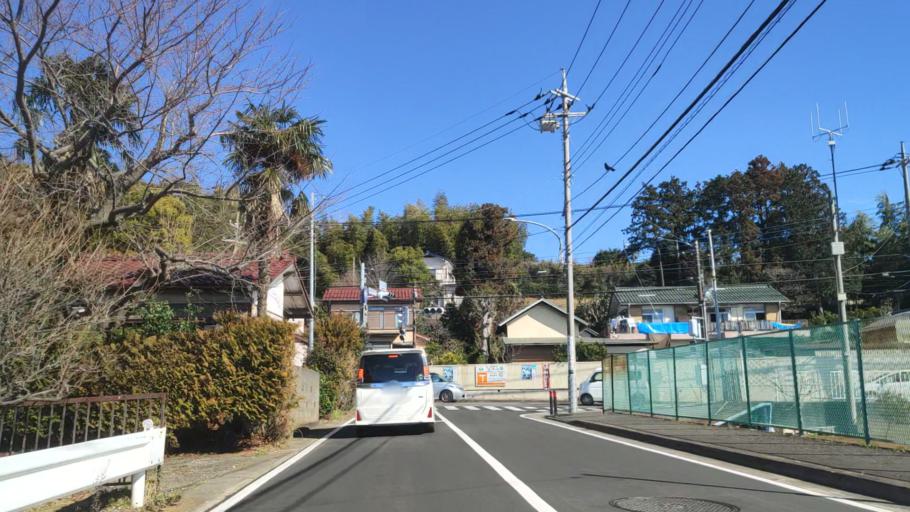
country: JP
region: Tokyo
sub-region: Machida-shi
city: Machida
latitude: 35.5200
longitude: 139.5374
